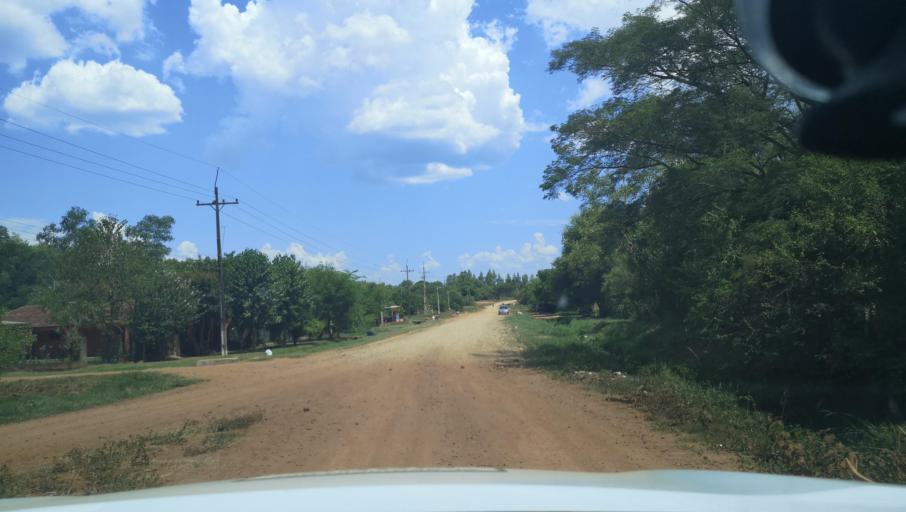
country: PY
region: Itapua
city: Carmen del Parana
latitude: -27.1680
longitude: -56.2491
